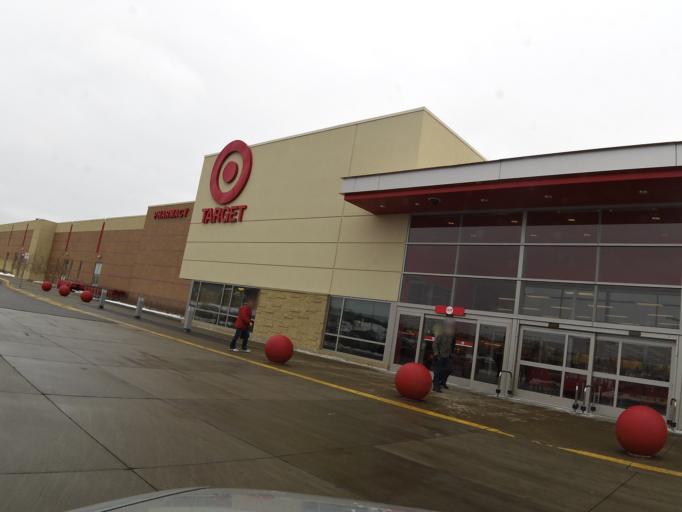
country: US
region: Minnesota
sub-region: Dakota County
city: Inver Grove Heights
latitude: 44.8358
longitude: -93.0879
